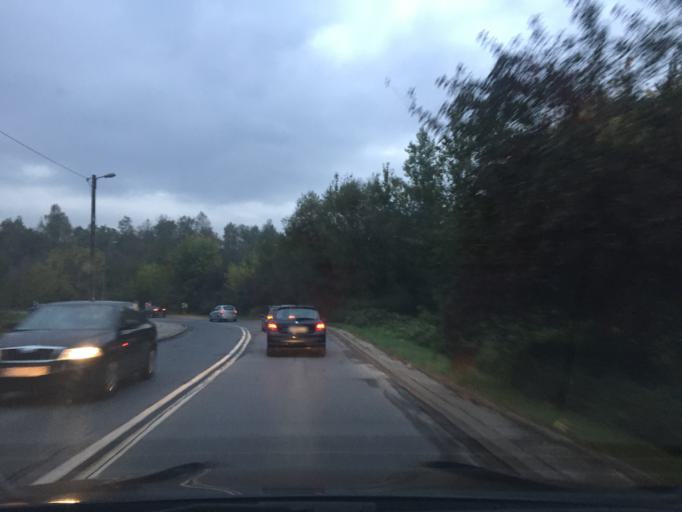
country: PL
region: Lesser Poland Voivodeship
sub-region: Powiat krakowski
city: Wrzasowice
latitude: 50.0064
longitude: 19.9371
